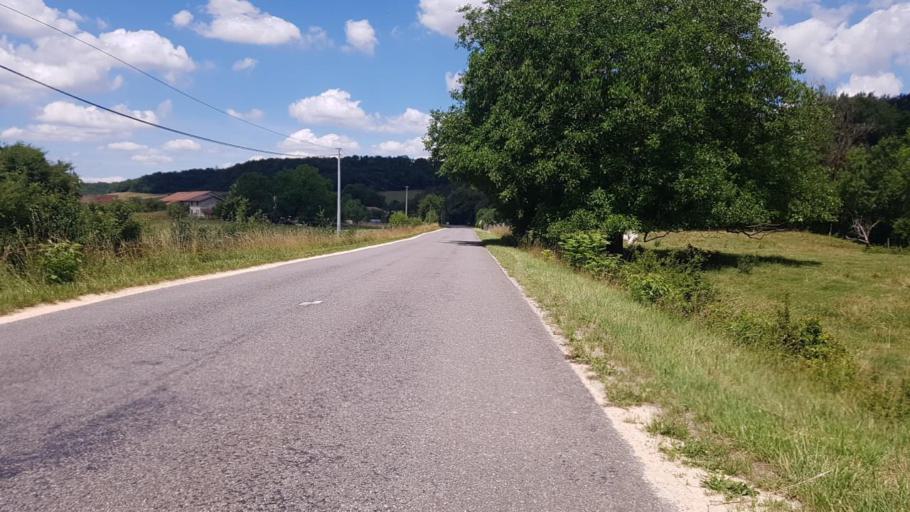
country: FR
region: Lorraine
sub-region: Departement de la Meuse
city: Ligny-en-Barrois
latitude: 48.6387
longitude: 5.4485
